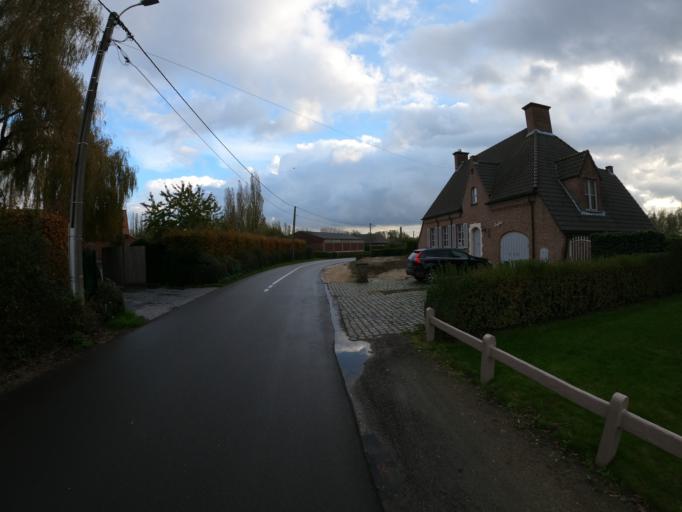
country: BE
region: Flanders
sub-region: Provincie Oost-Vlaanderen
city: Hamme
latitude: 51.1210
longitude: 4.1624
